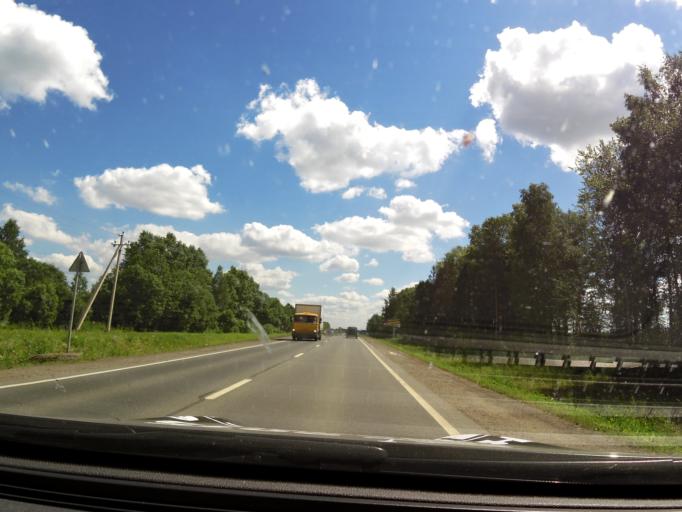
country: RU
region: Vologda
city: Molochnoye
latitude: 59.2546
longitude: 39.7610
